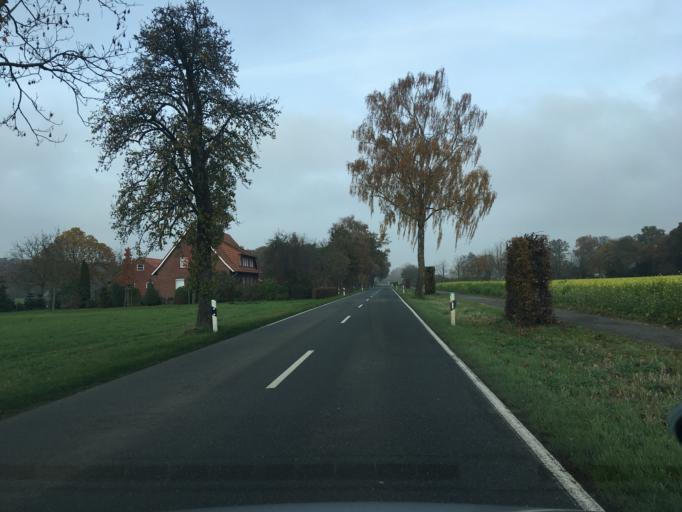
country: DE
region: North Rhine-Westphalia
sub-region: Regierungsbezirk Munster
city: Sudlohn
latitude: 51.9190
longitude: 6.9158
